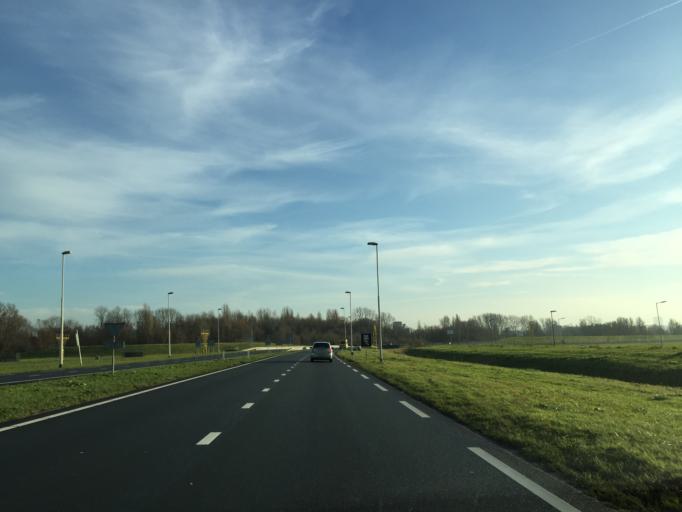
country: NL
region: South Holland
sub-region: Gemeente Lansingerland
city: Berkel en Rodenrijs
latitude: 51.9656
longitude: 4.4589
